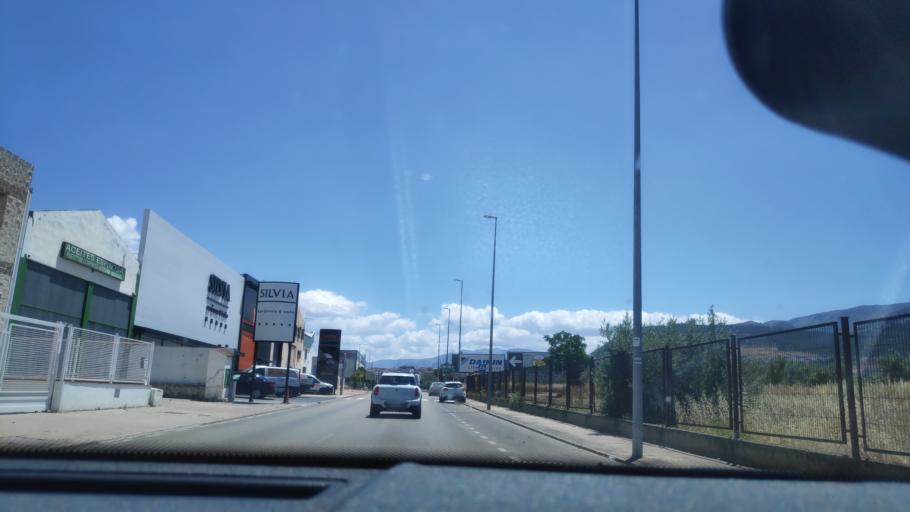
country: ES
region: Andalusia
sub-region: Provincia de Jaen
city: Jaen
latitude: 37.7957
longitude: -3.7928
